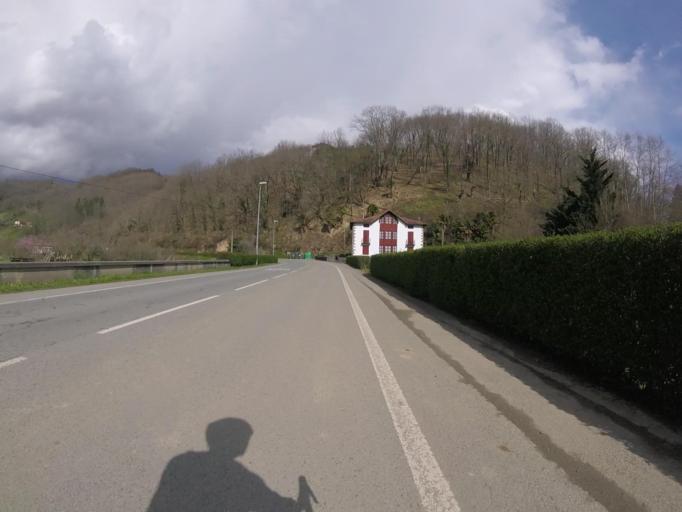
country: ES
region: Navarre
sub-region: Provincia de Navarra
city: Etxalar
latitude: 43.2348
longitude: -1.6390
